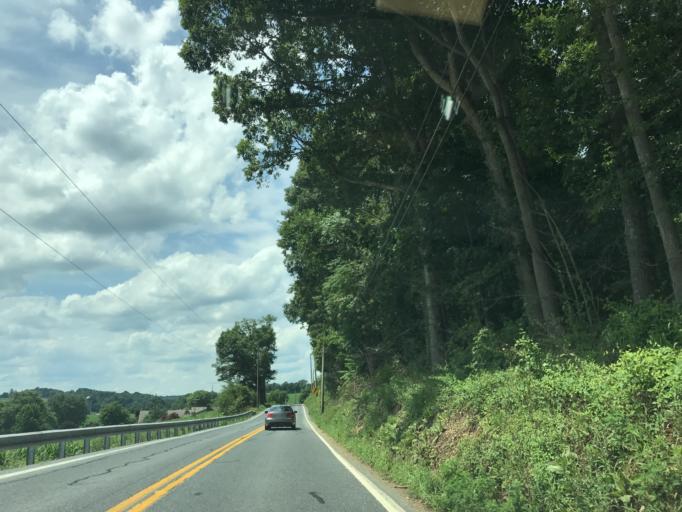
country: US
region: Pennsylvania
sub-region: Lancaster County
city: Brickerville
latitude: 40.2081
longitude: -76.3043
